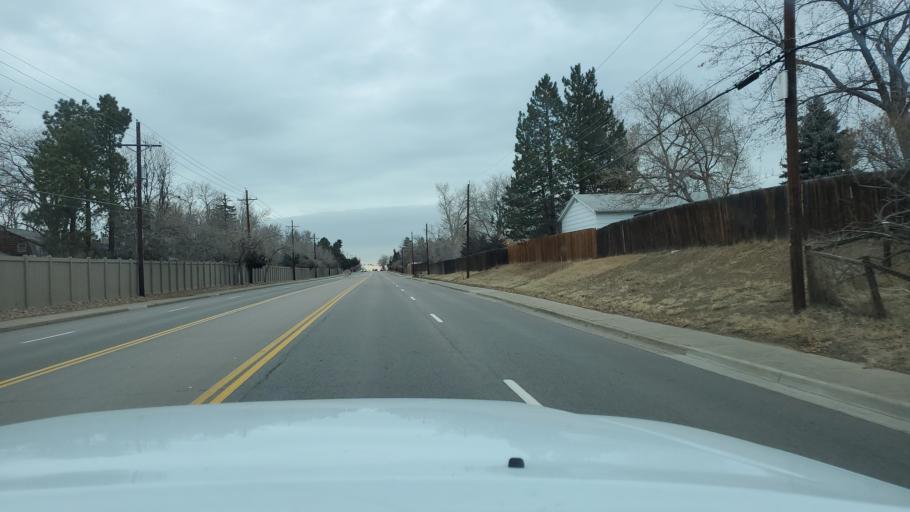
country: US
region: Colorado
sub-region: Arapahoe County
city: Southglenn
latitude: 39.5892
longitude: -104.9415
